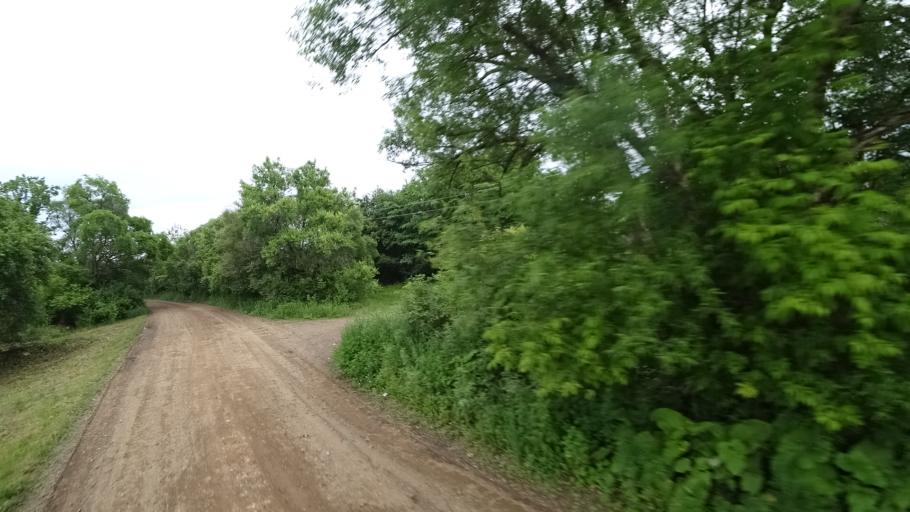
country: RU
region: Primorskiy
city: Novosysoyevka
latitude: 44.2411
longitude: 133.3749
